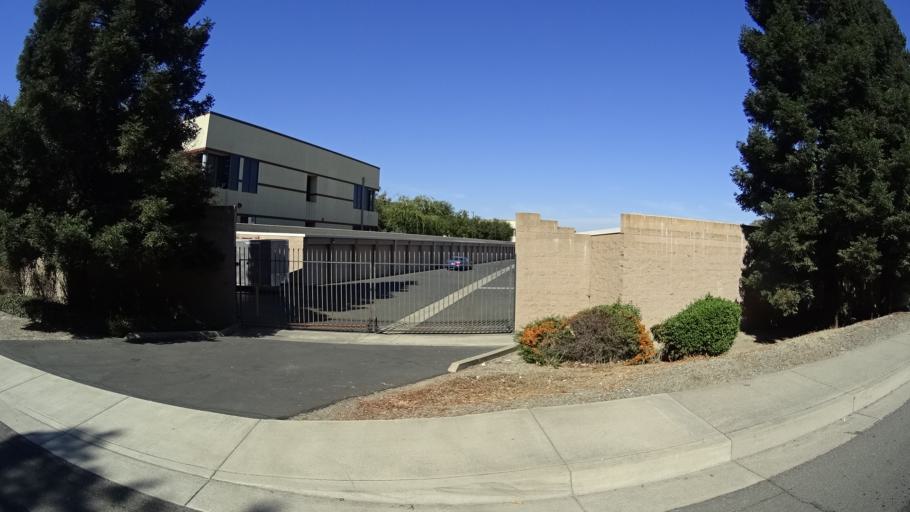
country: US
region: California
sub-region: Sacramento County
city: Parkway
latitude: 38.4885
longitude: -121.5153
